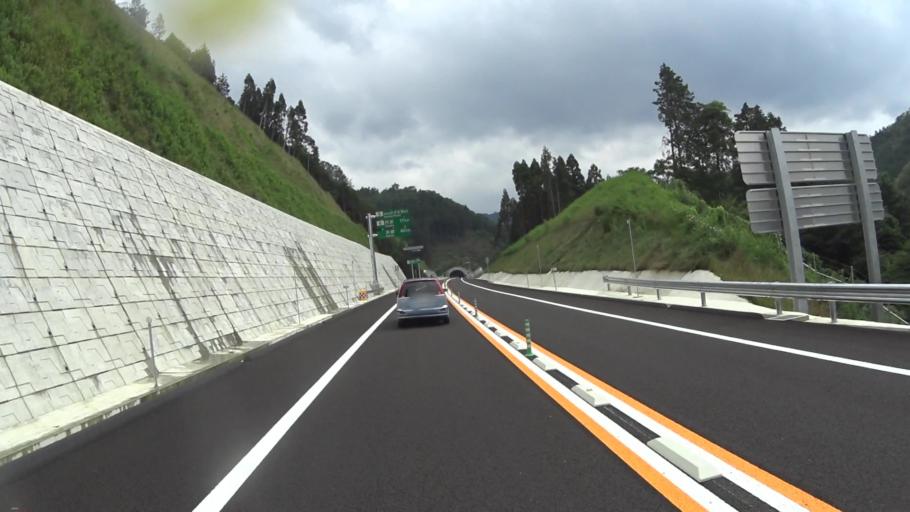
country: JP
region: Kyoto
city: Ayabe
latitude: 35.2623
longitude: 135.3453
